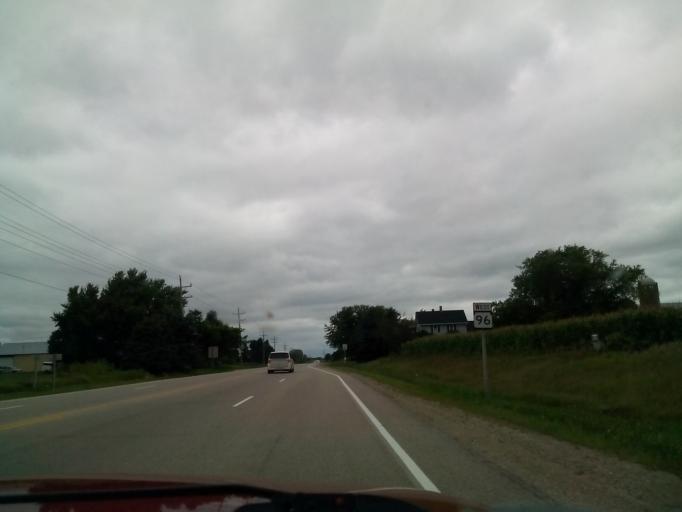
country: US
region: Wisconsin
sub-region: Outagamie County
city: Hortonville
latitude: 44.2724
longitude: -88.7404
